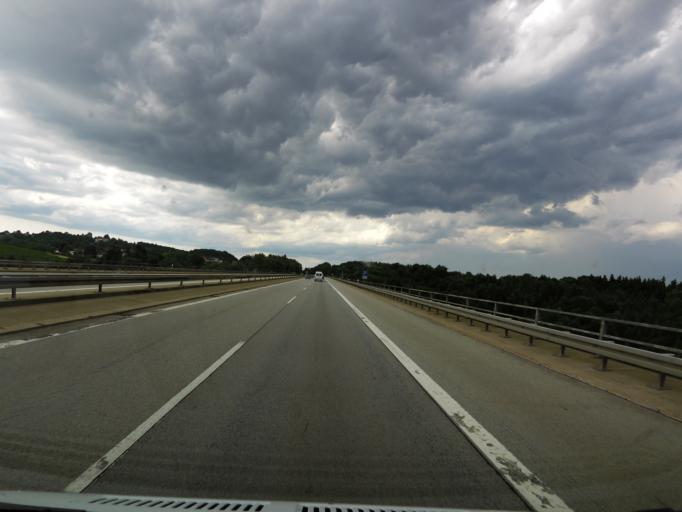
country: DE
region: Bavaria
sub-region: Lower Bavaria
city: Iggensbach
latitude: 48.7132
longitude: 13.1627
